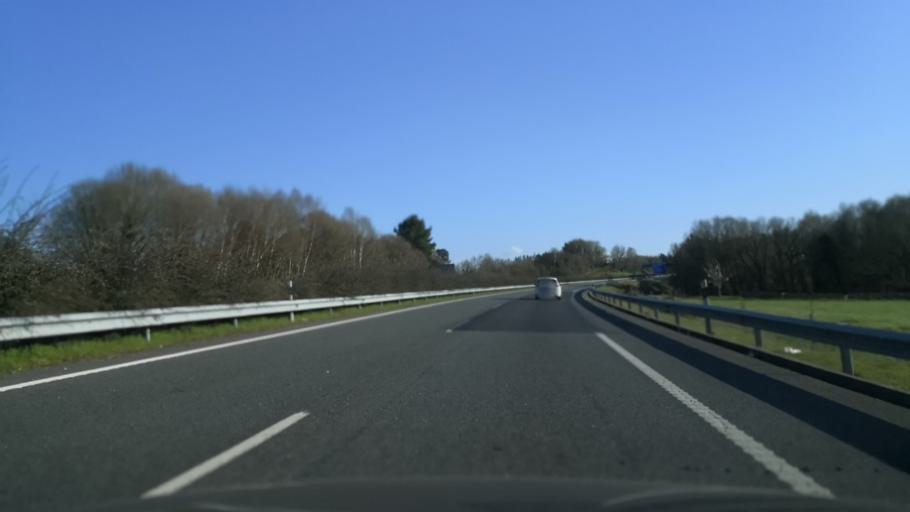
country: ES
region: Galicia
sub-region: Provincia de Lugo
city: Lugo
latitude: 42.9860
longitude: -7.5021
